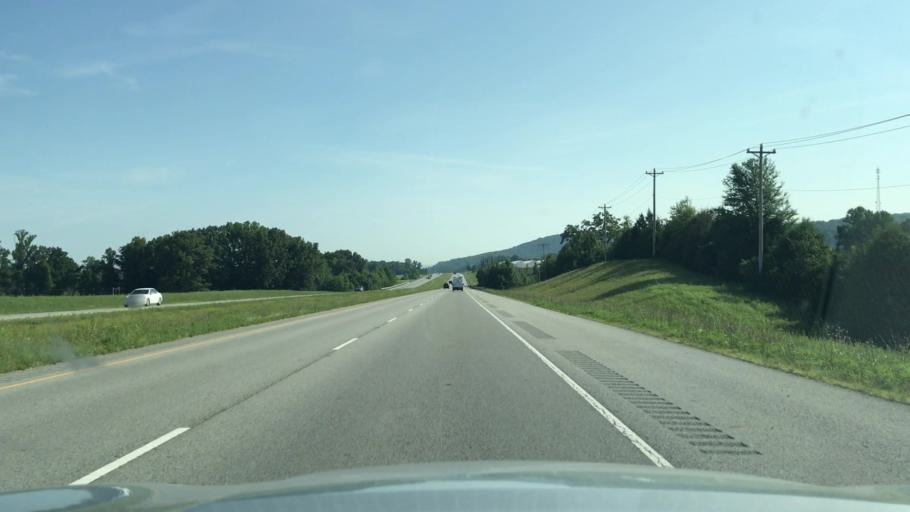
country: US
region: Tennessee
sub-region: Overton County
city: Livingston
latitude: 36.2854
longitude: -85.3749
